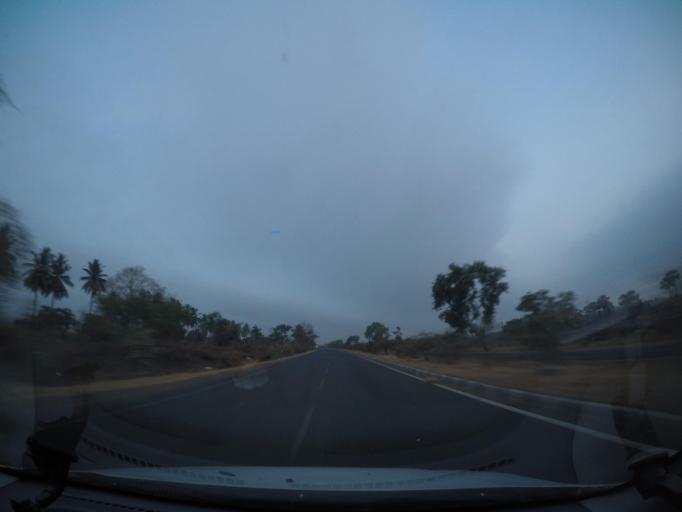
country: IN
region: Andhra Pradesh
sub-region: West Godavari
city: Tadepallegudem
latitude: 16.8173
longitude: 81.3868
